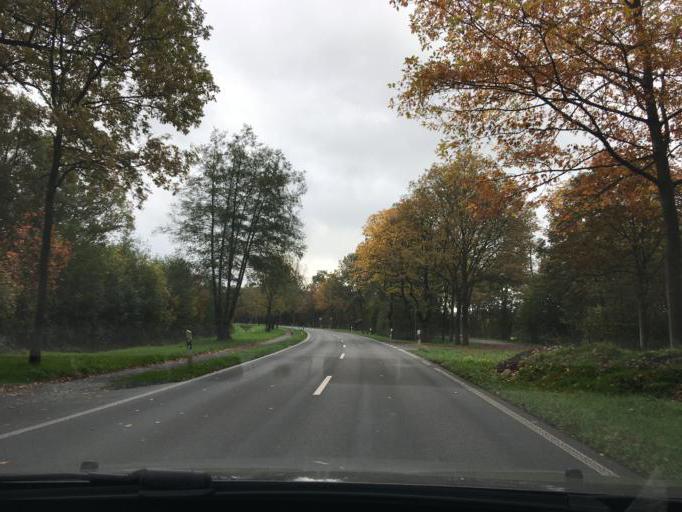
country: DE
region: North Rhine-Westphalia
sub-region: Regierungsbezirk Munster
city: Vreden
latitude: 52.0718
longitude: 6.7848
